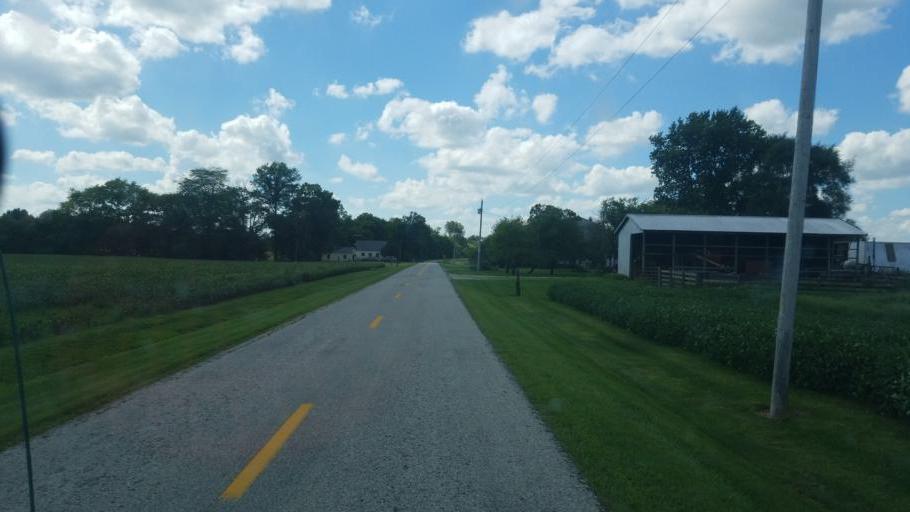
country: US
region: Ohio
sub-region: Union County
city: Richwood
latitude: 40.3506
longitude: -83.2341
